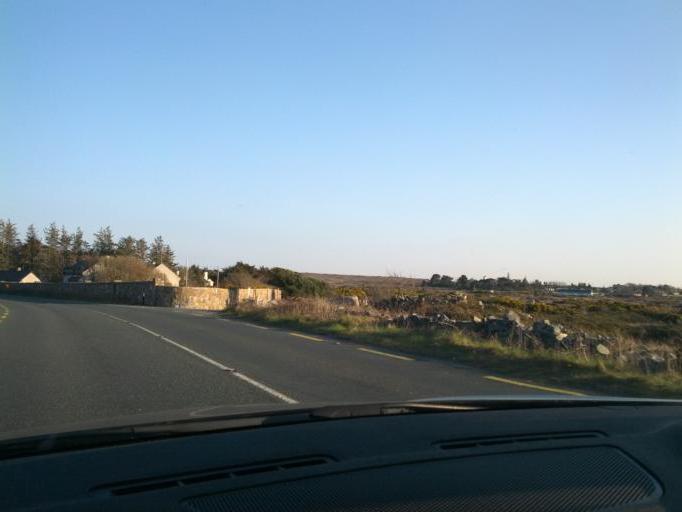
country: IE
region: Connaught
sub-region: County Galway
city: Oughterard
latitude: 53.2815
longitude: -9.5391
